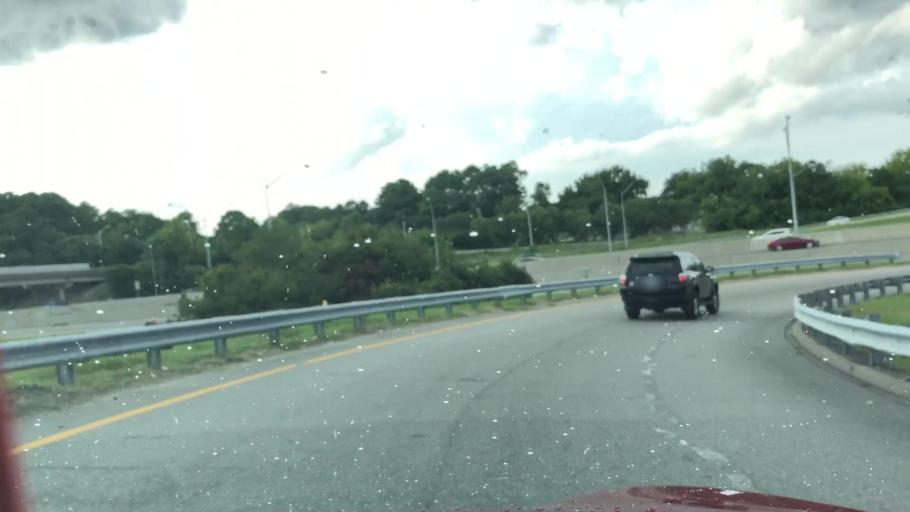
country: US
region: Virginia
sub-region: City of Chesapeake
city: Chesapeake
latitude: 36.8423
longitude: -76.2114
